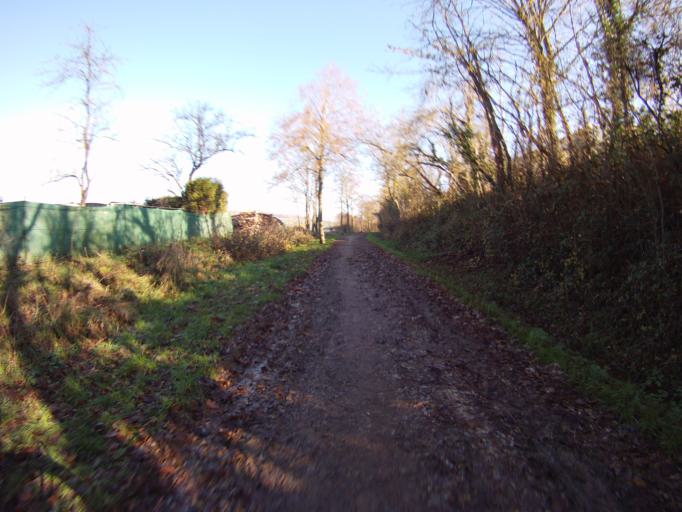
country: FR
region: Lorraine
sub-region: Departement de Meurthe-et-Moselle
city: Faulx
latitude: 48.7917
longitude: 6.2047
